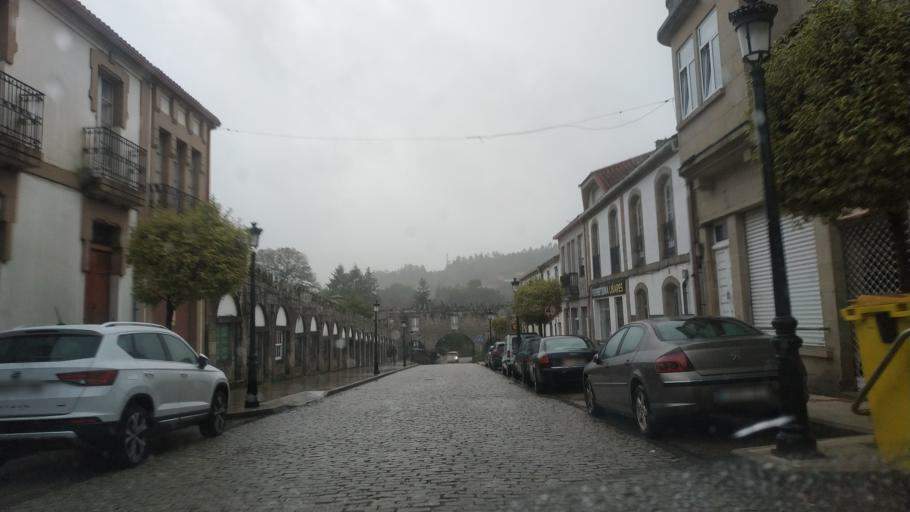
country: ES
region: Galicia
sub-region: Provincia da Coruna
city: Negreira
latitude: 42.9084
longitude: -8.7378
